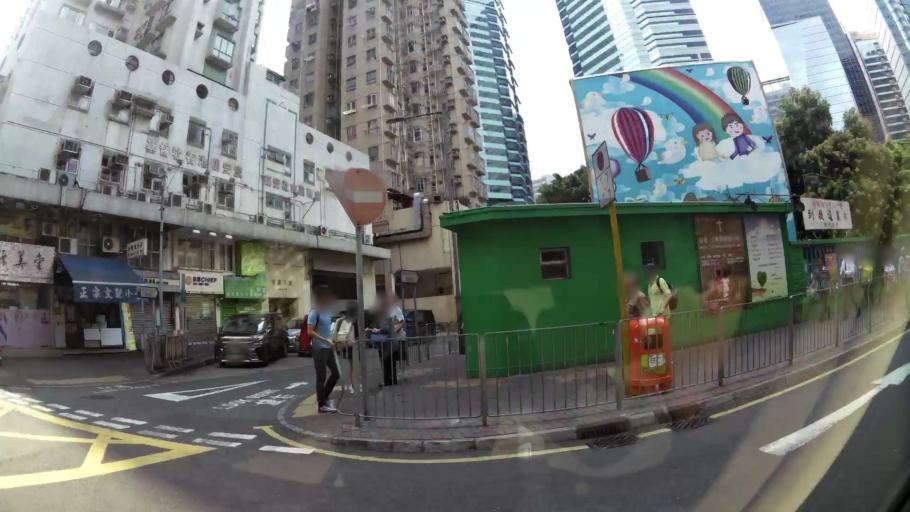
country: HK
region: Kowloon City
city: Kowloon
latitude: 22.3149
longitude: 114.2220
